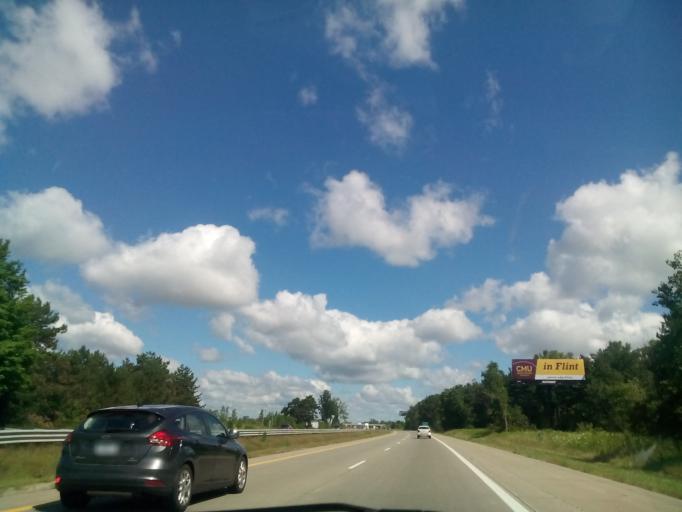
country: US
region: Michigan
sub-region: Genesee County
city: Flint
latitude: 42.9355
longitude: -83.7233
